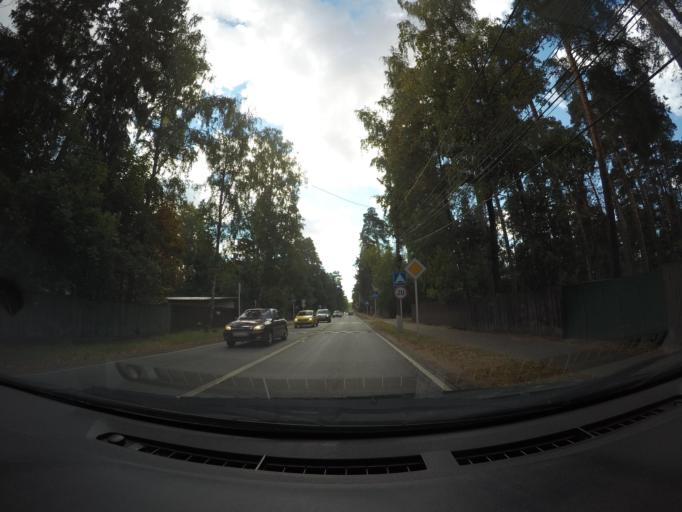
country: RU
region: Moskovskaya
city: Il'inskiy
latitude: 55.6255
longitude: 38.1114
